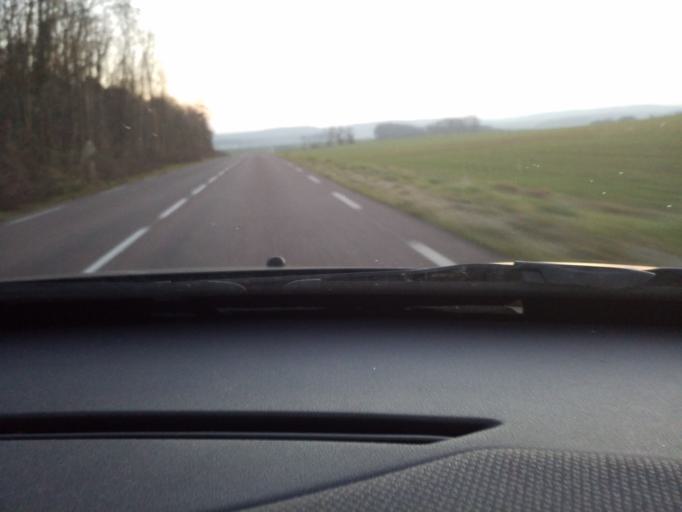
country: FR
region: Franche-Comte
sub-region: Departement de la Haute-Saone
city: Faverney
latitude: 47.8984
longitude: 6.0746
